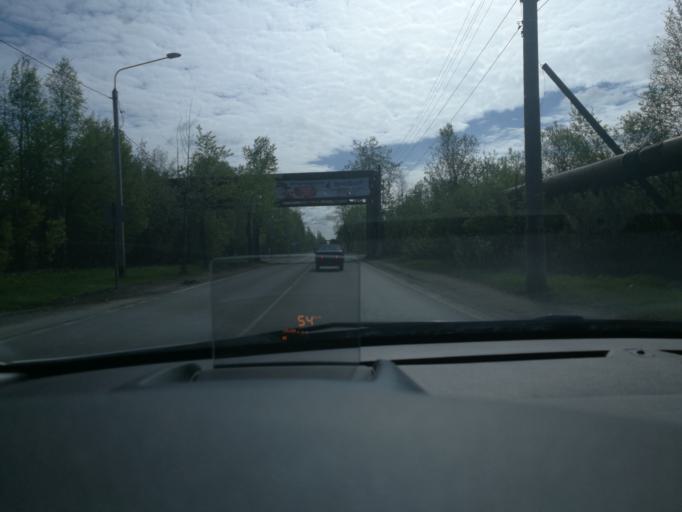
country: RU
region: Arkhangelskaya
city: Arkhangel'sk
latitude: 64.5957
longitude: 40.5711
